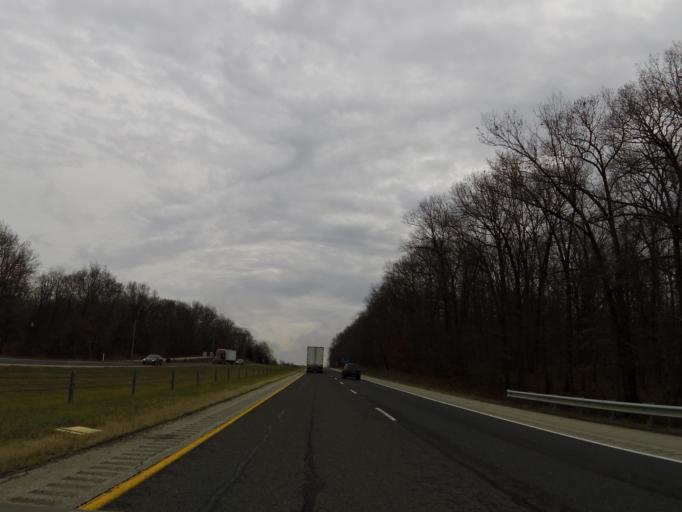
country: US
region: Indiana
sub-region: Ripley County
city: Sunman
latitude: 39.2803
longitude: -85.1129
